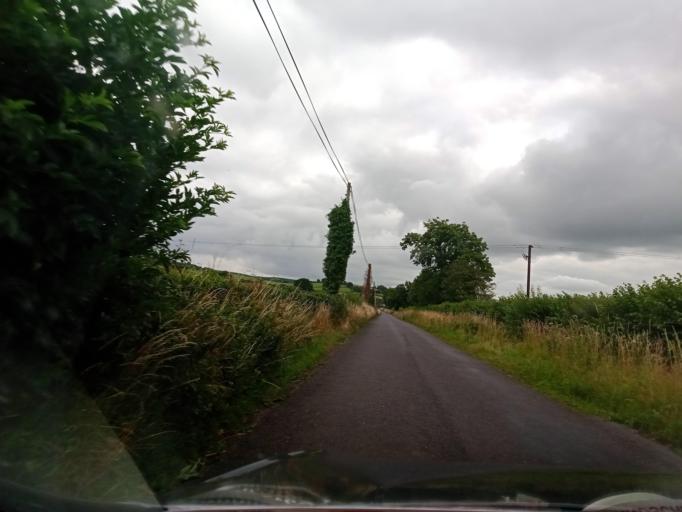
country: IE
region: Leinster
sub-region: Laois
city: Stradbally
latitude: 52.9857
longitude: -7.1726
